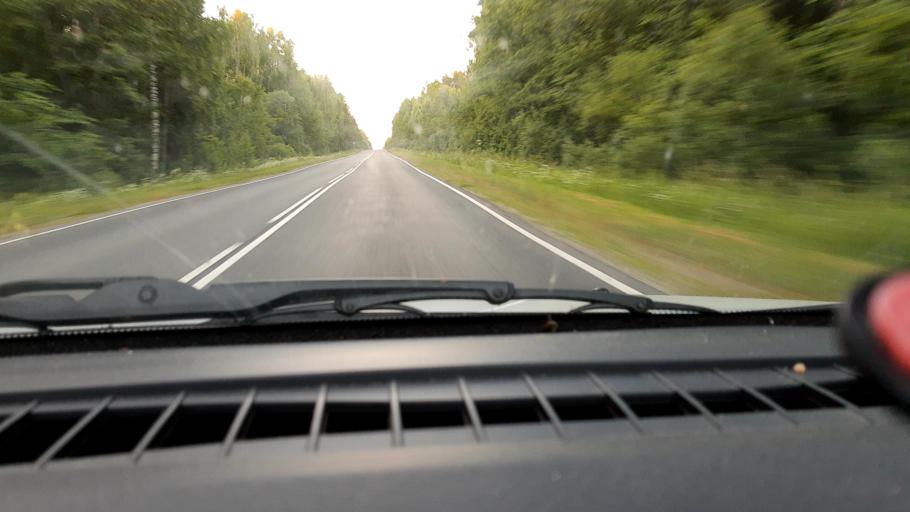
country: RU
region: Nizjnij Novgorod
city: Uren'
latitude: 57.2676
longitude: 45.6231
